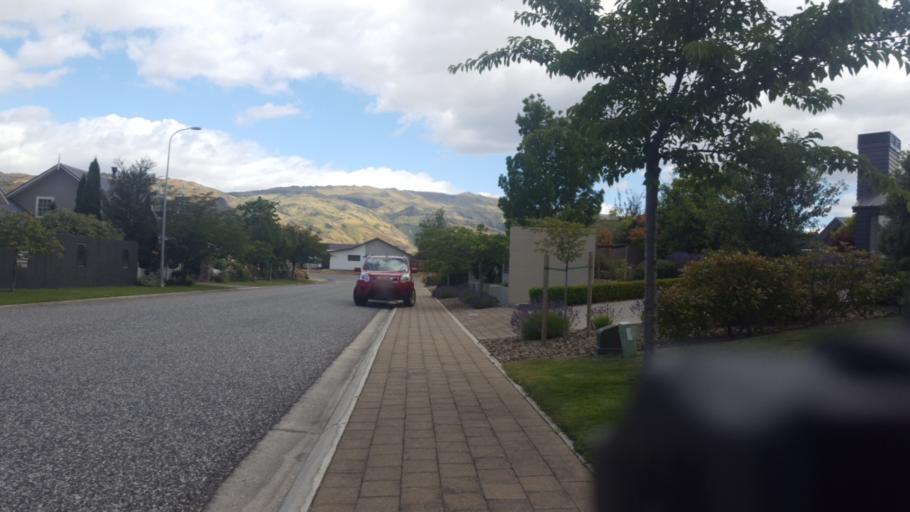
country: NZ
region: Otago
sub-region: Queenstown-Lakes District
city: Wanaka
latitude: -45.1969
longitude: 169.3332
